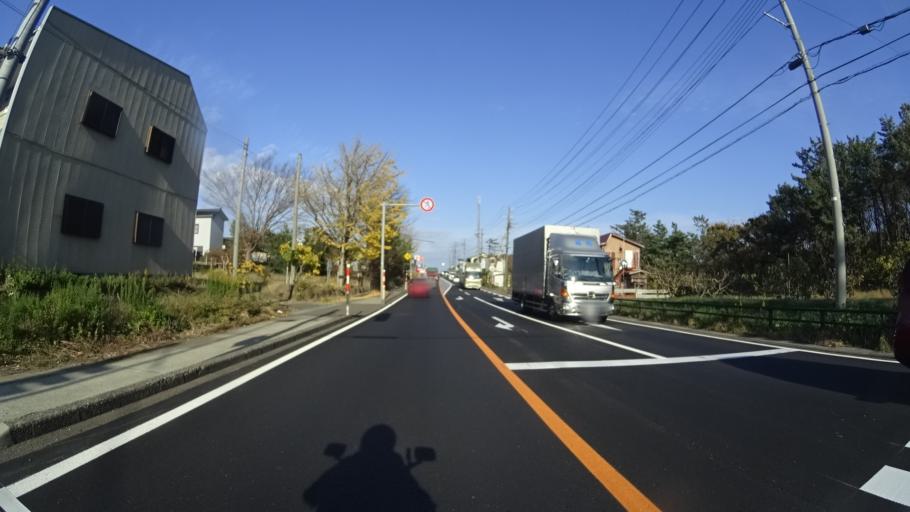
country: JP
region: Niigata
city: Joetsu
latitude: 37.2370
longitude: 138.3411
